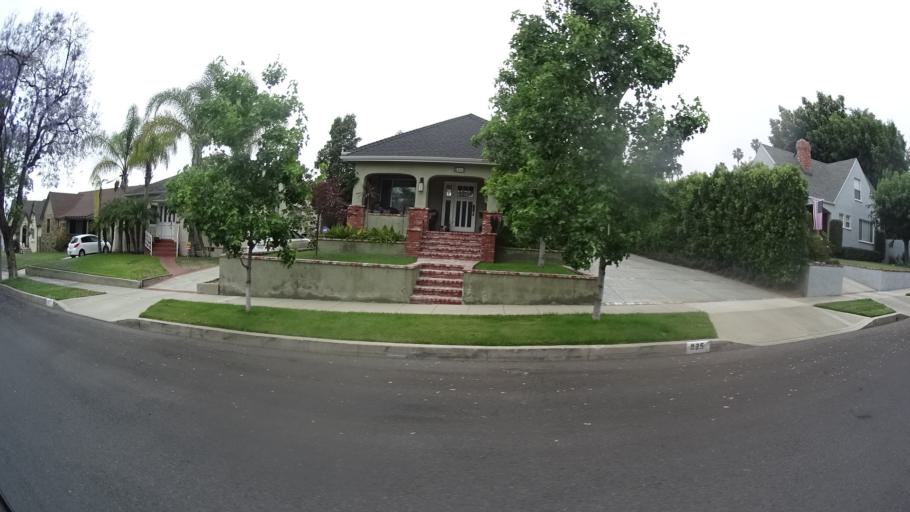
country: US
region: California
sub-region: Los Angeles County
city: Burbank
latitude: 34.1867
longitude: -118.2956
